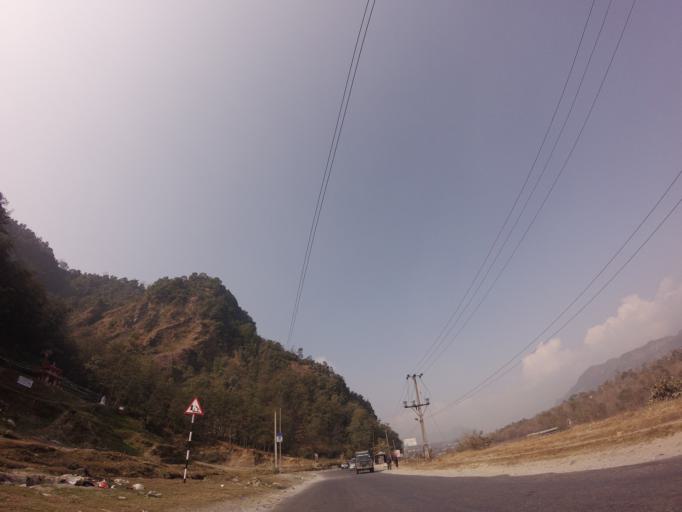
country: NP
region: Western Region
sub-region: Gandaki Zone
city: Pokhara
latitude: 28.2487
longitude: 83.9744
